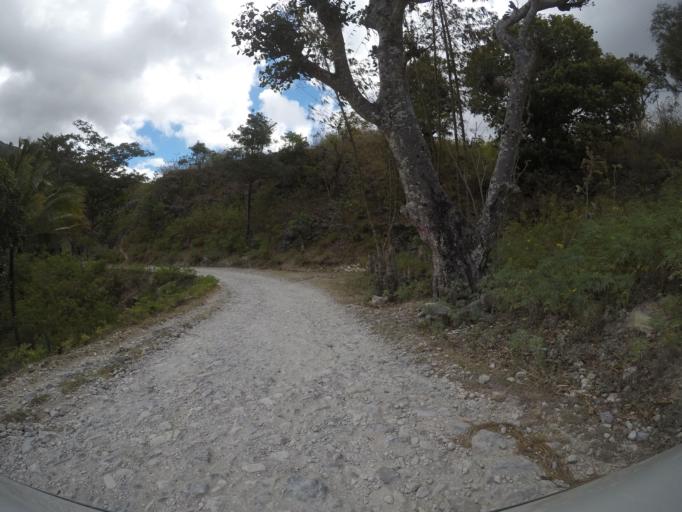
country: TL
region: Baucau
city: Baucau
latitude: -8.5249
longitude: 126.6907
